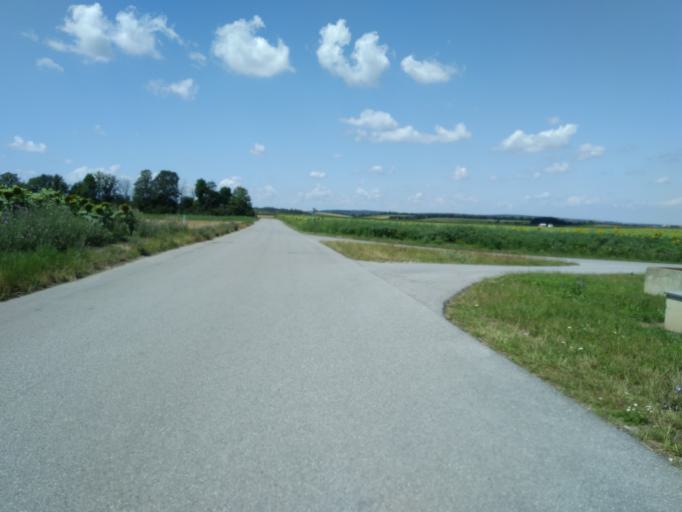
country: AT
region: Lower Austria
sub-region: Politischer Bezirk Ganserndorf
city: Auersthal
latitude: 48.3758
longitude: 16.6734
